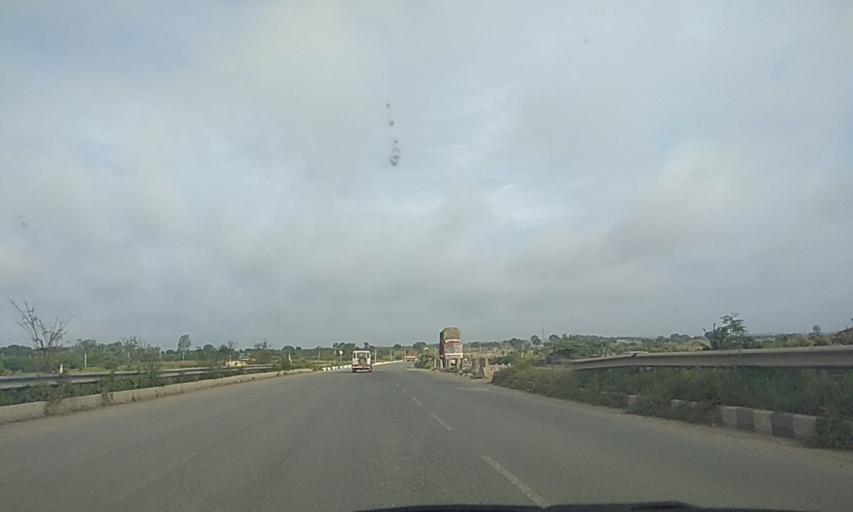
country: IN
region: Karnataka
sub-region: Haveri
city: Haveri
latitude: 14.7638
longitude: 75.4316
